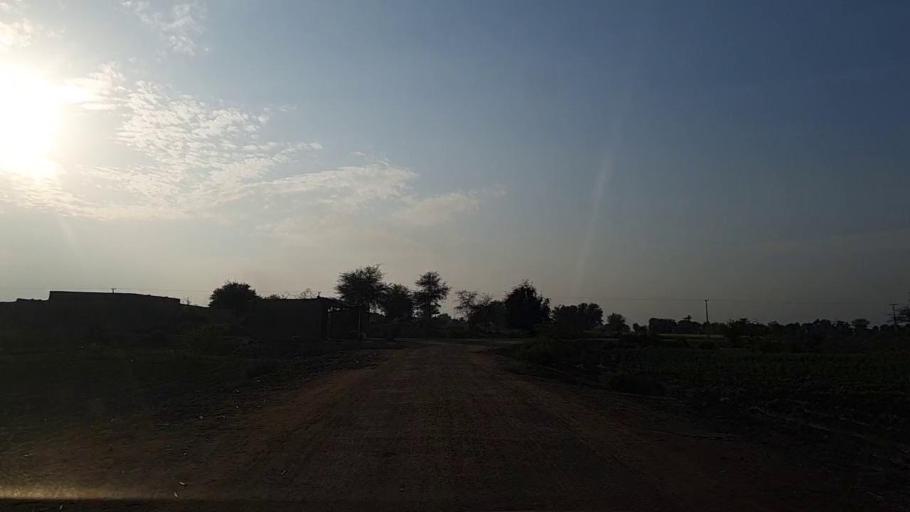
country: PK
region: Sindh
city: Jam Sahib
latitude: 26.3943
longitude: 68.5207
